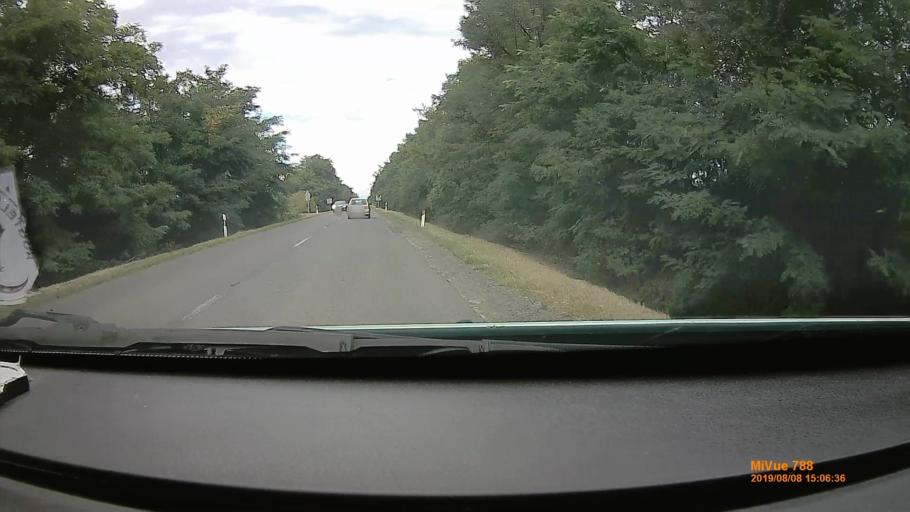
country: HU
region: Szabolcs-Szatmar-Bereg
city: Tunyogmatolcs
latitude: 47.9496
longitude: 22.4322
